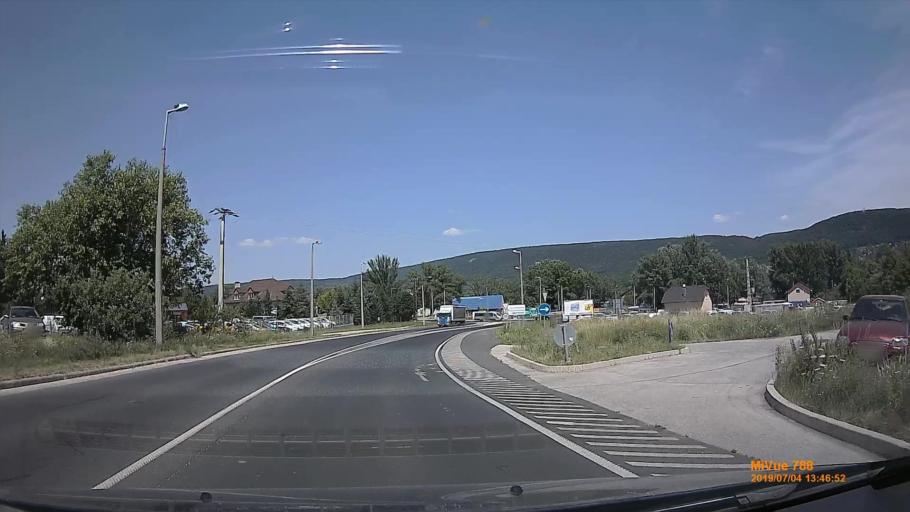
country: HU
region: Komarom-Esztergom
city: Tatabanya
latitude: 47.5910
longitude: 18.3795
